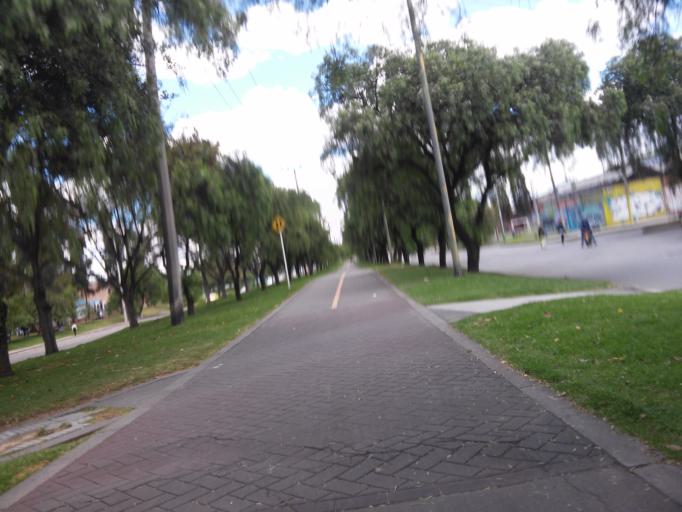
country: CO
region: Bogota D.C.
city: Bogota
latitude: 4.6230
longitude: -74.1064
